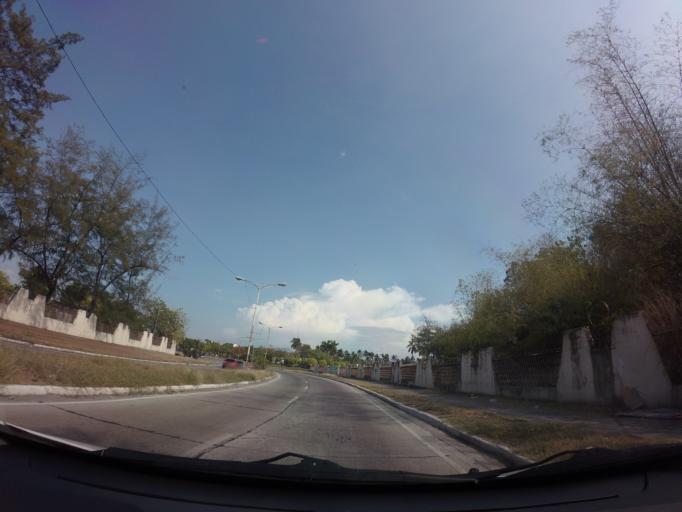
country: PH
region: Calabarzon
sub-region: Province of Rizal
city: Pateros
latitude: 14.5203
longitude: 121.0468
